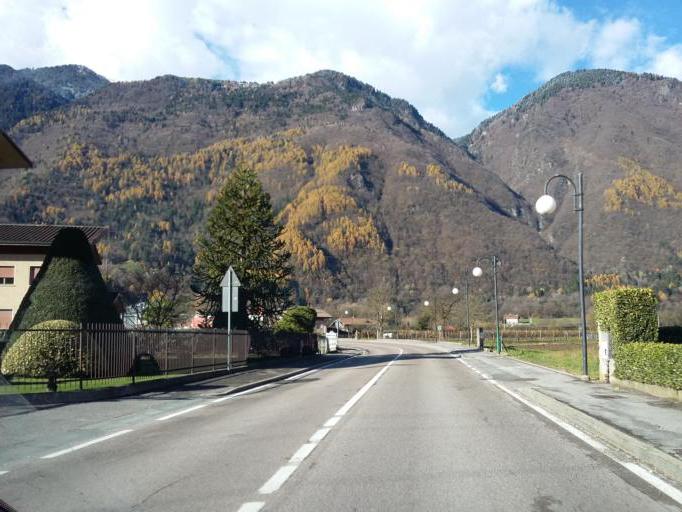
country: IT
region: Trentino-Alto Adige
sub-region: Provincia di Trento
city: Storo
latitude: 45.8536
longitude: 10.5729
